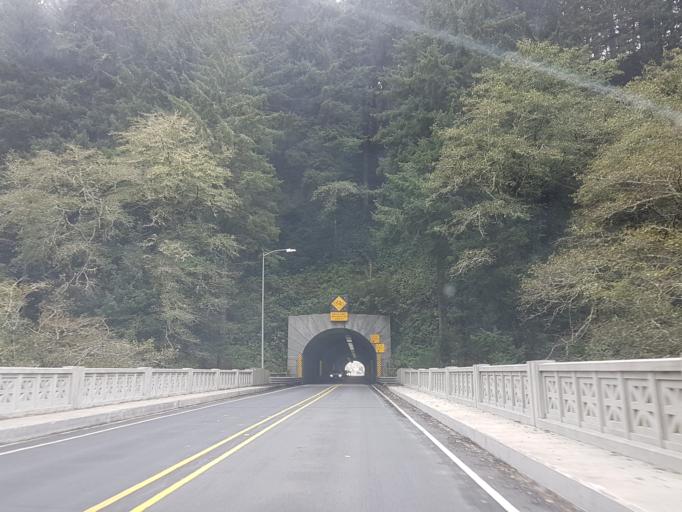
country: US
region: Oregon
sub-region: Lane County
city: Florence
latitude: 44.1332
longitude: -124.1219
